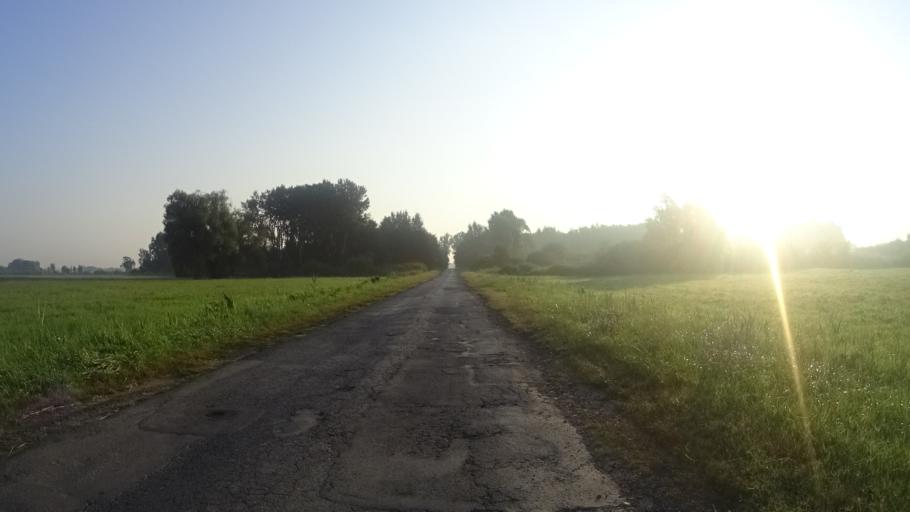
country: HU
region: Zala
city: Zalakomar
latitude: 46.5424
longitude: 17.1572
